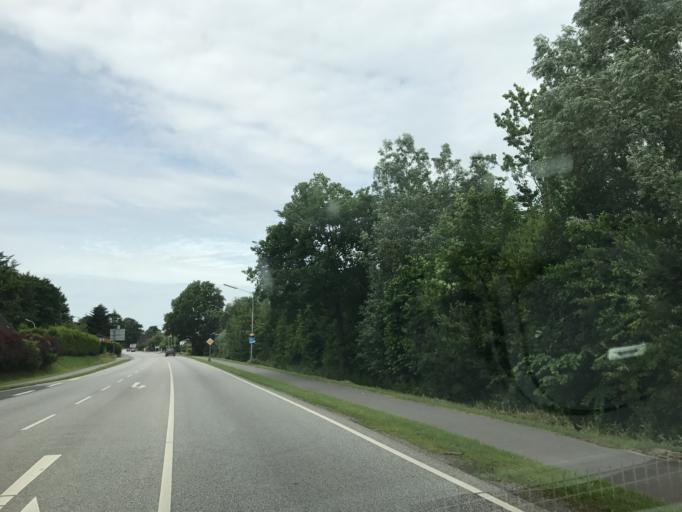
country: DE
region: Schleswig-Holstein
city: Nindorf
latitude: 54.0877
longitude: 9.1224
